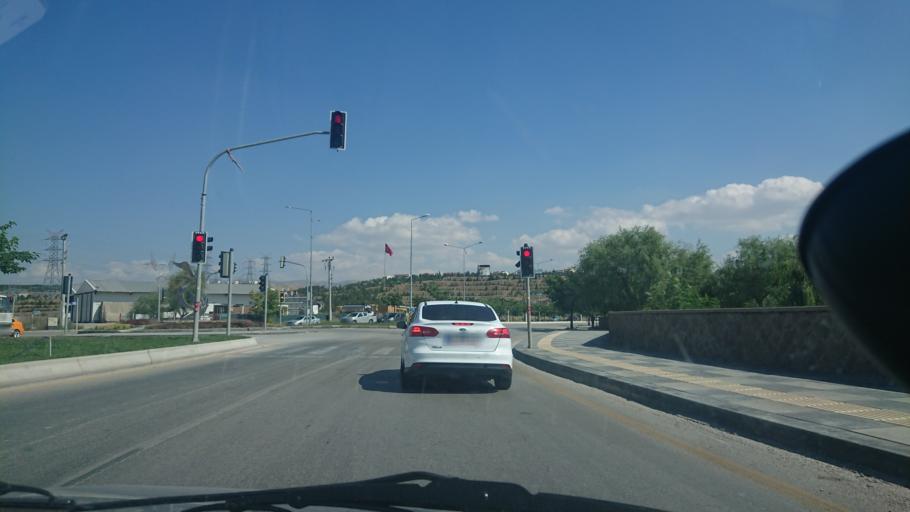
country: TR
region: Ankara
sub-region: Goelbasi
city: Golbasi
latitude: 39.8035
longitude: 32.8078
